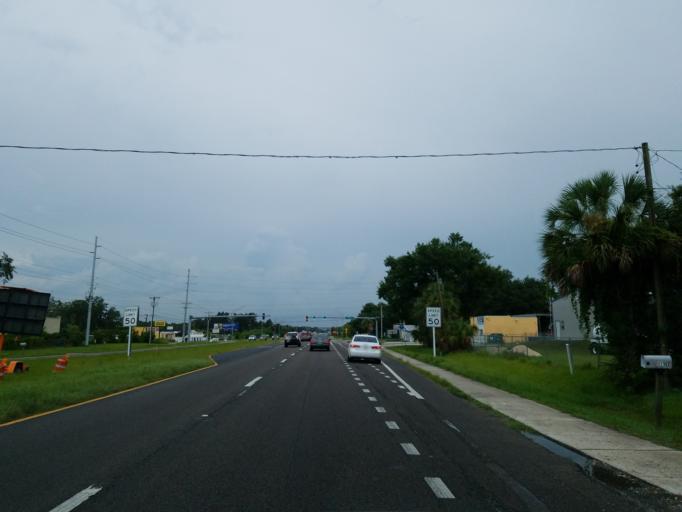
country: US
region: Florida
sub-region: Hillsborough County
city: Gibsonton
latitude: 27.8337
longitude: -82.3816
